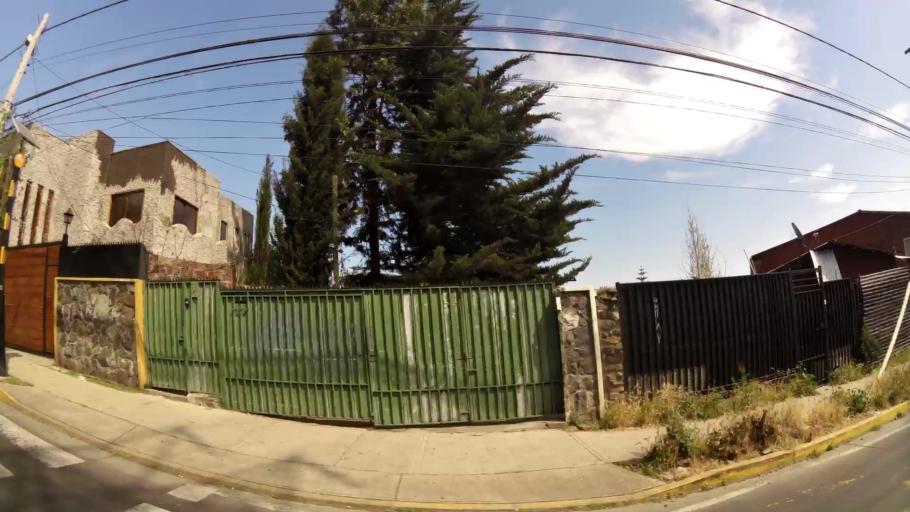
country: CL
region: Santiago Metropolitan
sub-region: Provincia de Santiago
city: Villa Presidente Frei, Nunoa, Santiago, Chile
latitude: -33.4677
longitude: -70.5302
